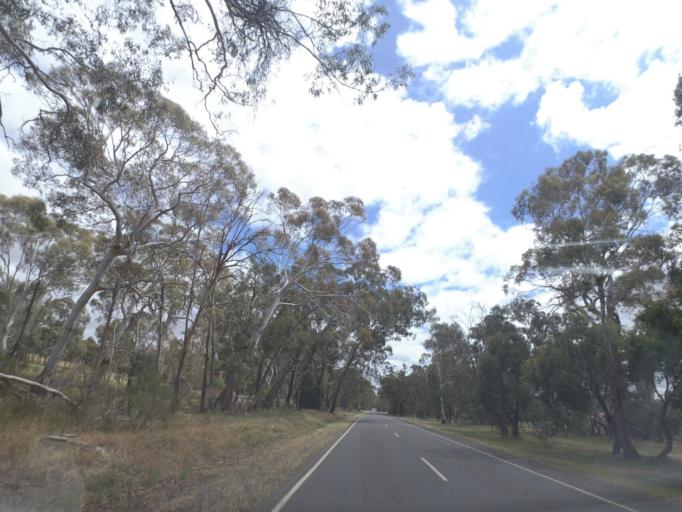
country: AU
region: Victoria
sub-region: Whittlesea
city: Whittlesea
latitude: -37.2540
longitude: 145.0484
